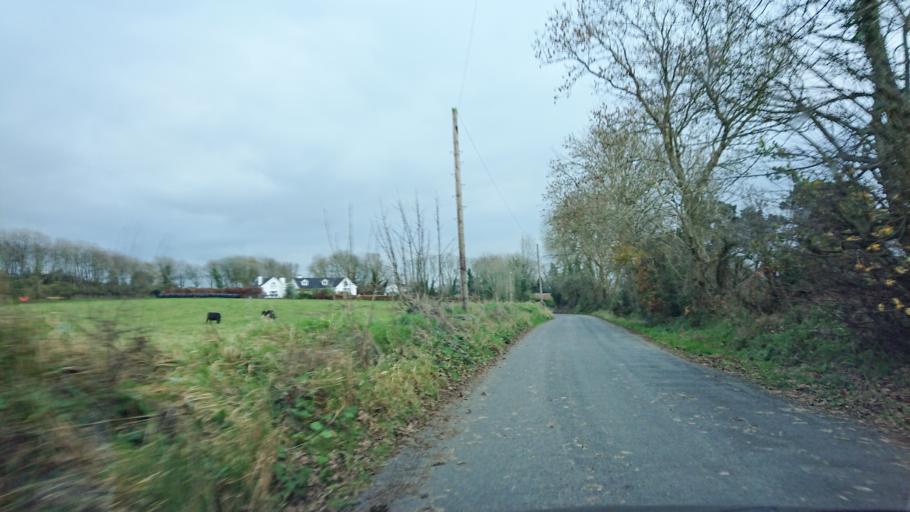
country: IE
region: Munster
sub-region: Waterford
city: Waterford
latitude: 52.2537
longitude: -7.0129
